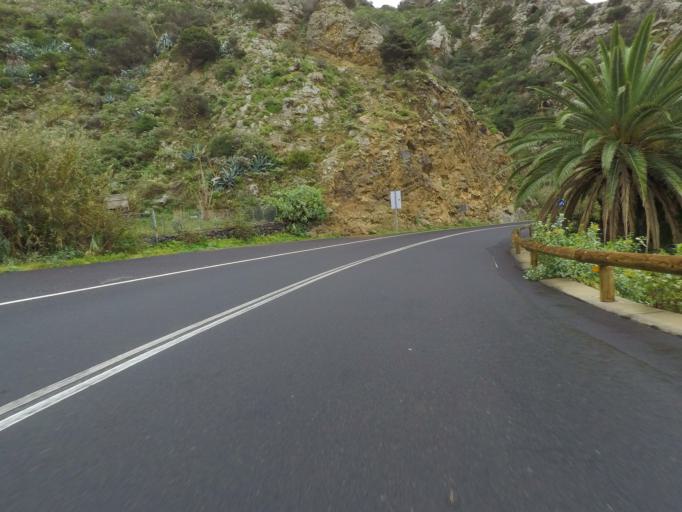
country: ES
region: Canary Islands
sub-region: Provincia de Santa Cruz de Tenerife
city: Vallehermosa
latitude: 28.1821
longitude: -17.2618
